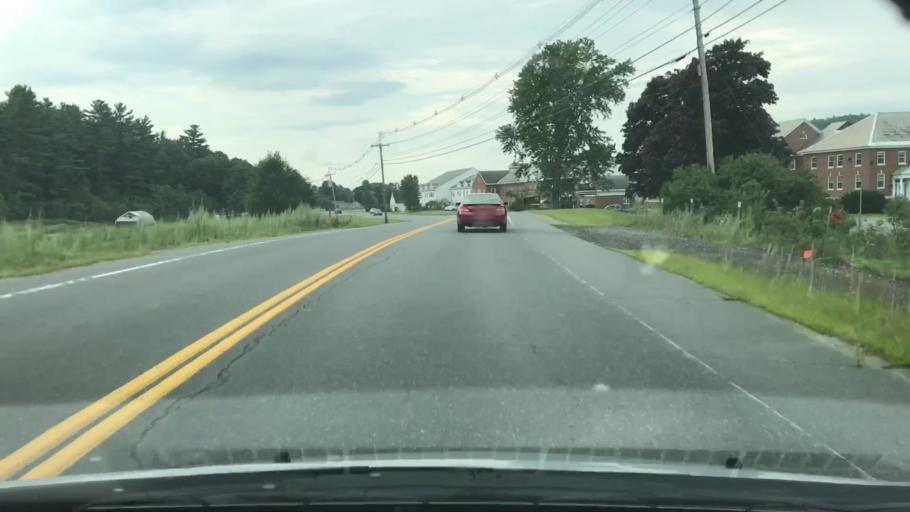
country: US
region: New Hampshire
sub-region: Grafton County
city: North Haverhill
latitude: 44.1169
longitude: -72.0394
